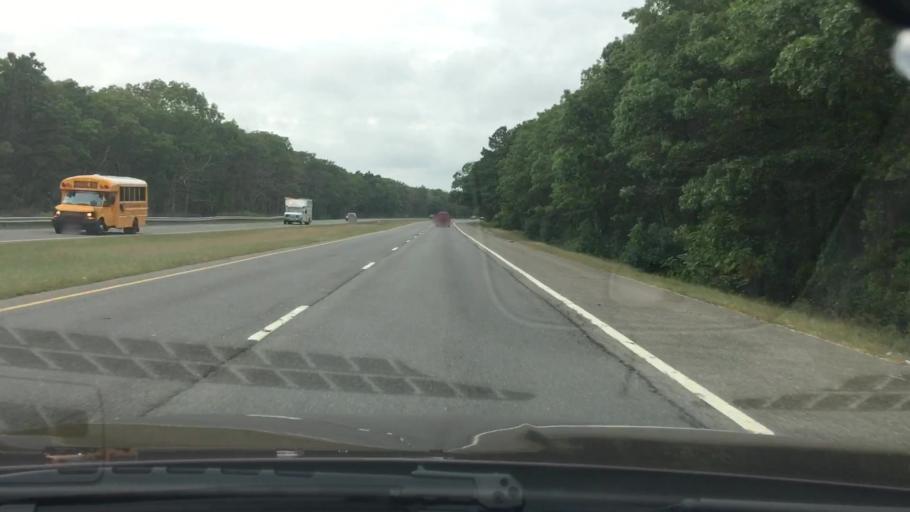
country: US
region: New York
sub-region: Suffolk County
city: Islandia
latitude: 40.7895
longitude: -73.1503
